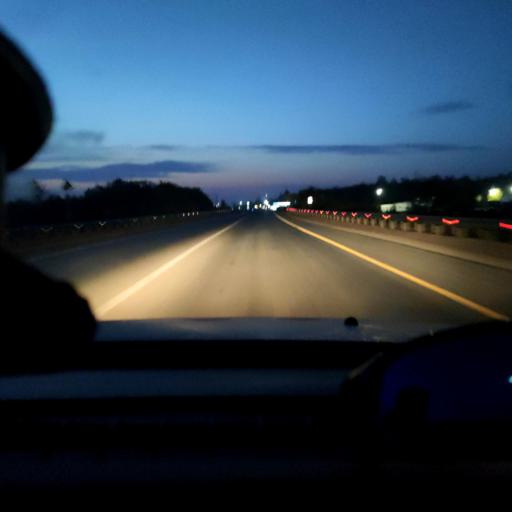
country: RU
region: Samara
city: Novokuybyshevsk
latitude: 53.0838
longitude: 50.0684
